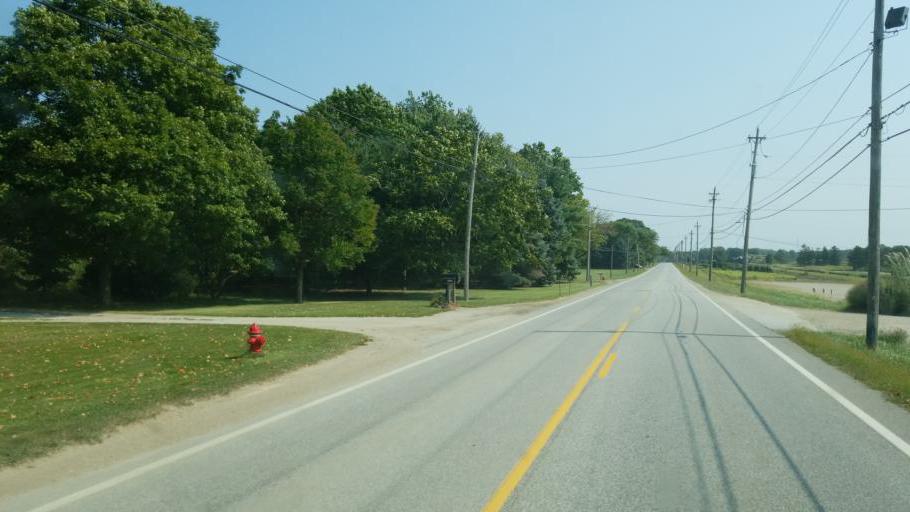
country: US
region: Ohio
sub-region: Lake County
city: Perry
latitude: 41.7373
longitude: -81.1657
